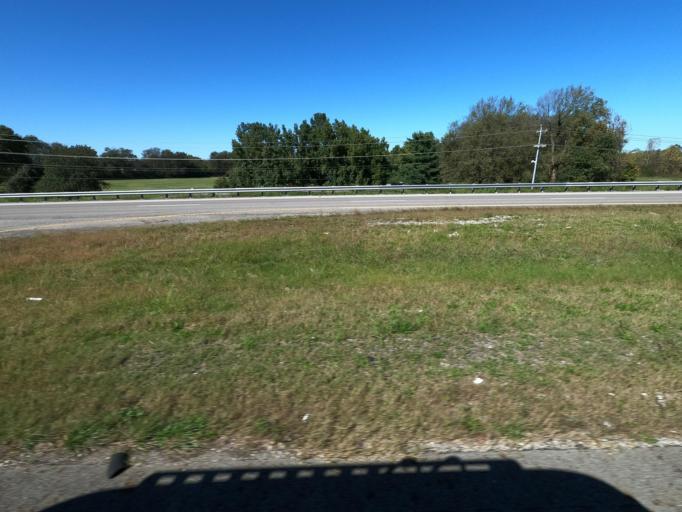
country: US
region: Tennessee
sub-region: Maury County
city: Mount Pleasant
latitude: 35.5635
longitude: -87.1754
